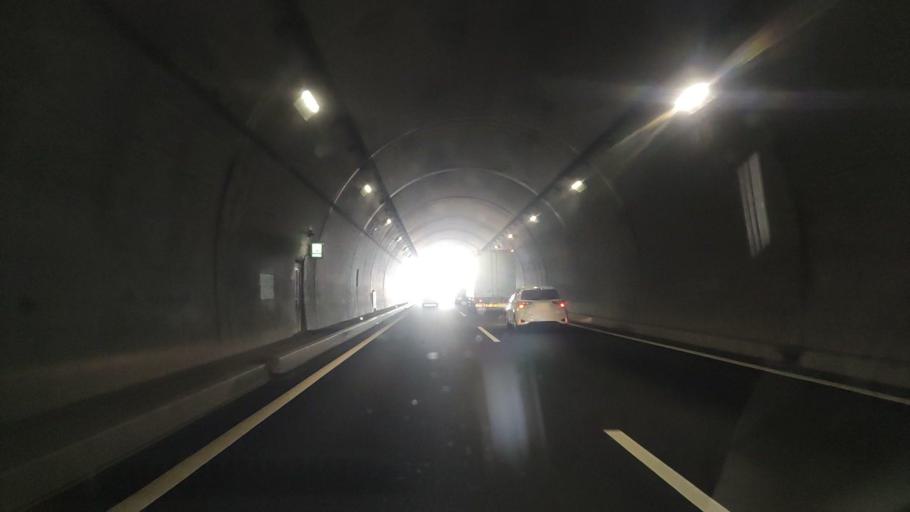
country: JP
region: Kanagawa
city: Zama
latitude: 35.5105
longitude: 139.3638
